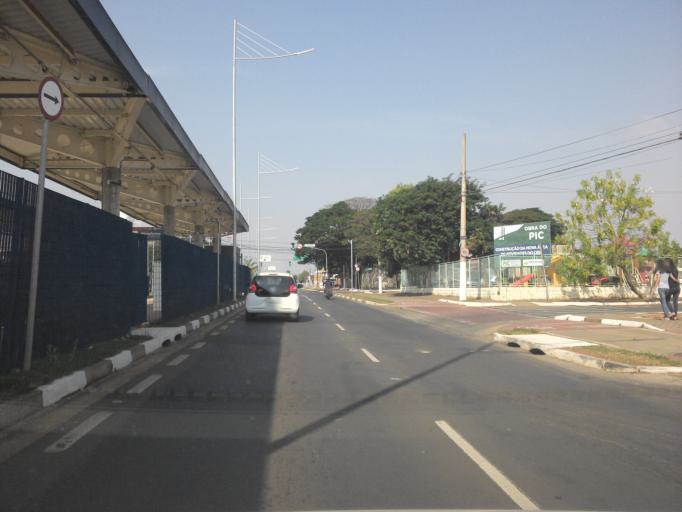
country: BR
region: Sao Paulo
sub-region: Hortolandia
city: Hortolandia
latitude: -22.8751
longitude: -47.2065
